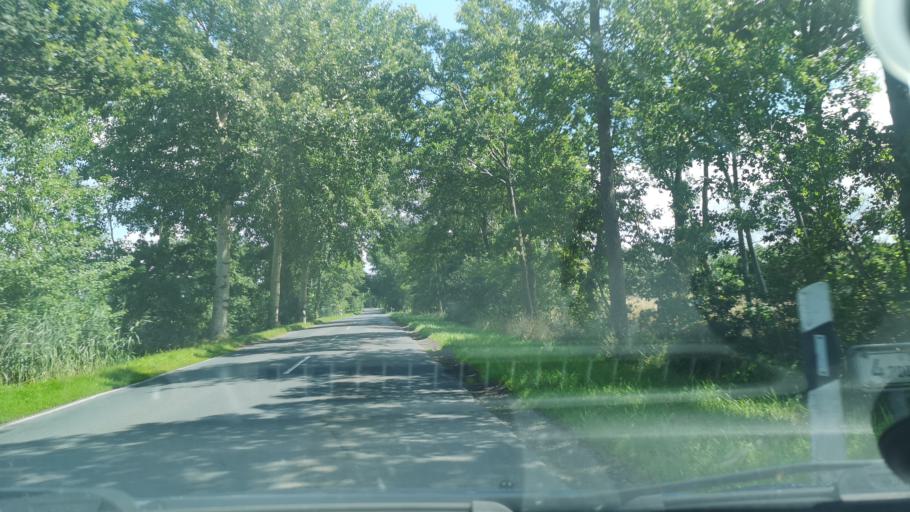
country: DE
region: Lower Saxony
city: Mulsum
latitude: 53.6426
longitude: 8.5810
